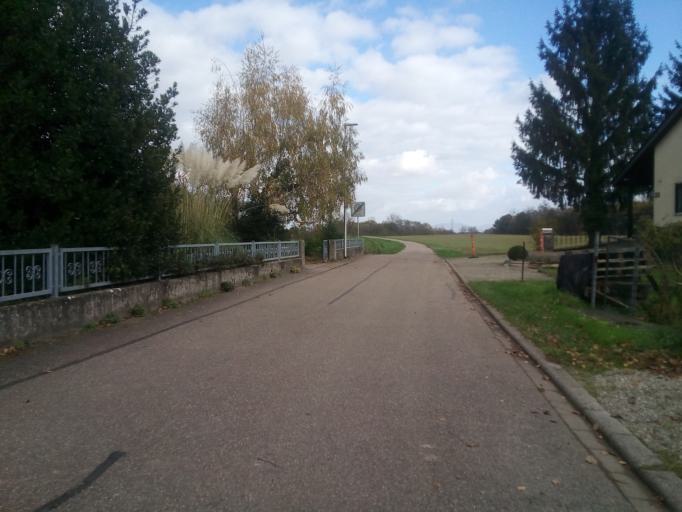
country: DE
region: Baden-Wuerttemberg
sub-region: Karlsruhe Region
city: Lichtenau
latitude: 48.7121
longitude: 7.9679
